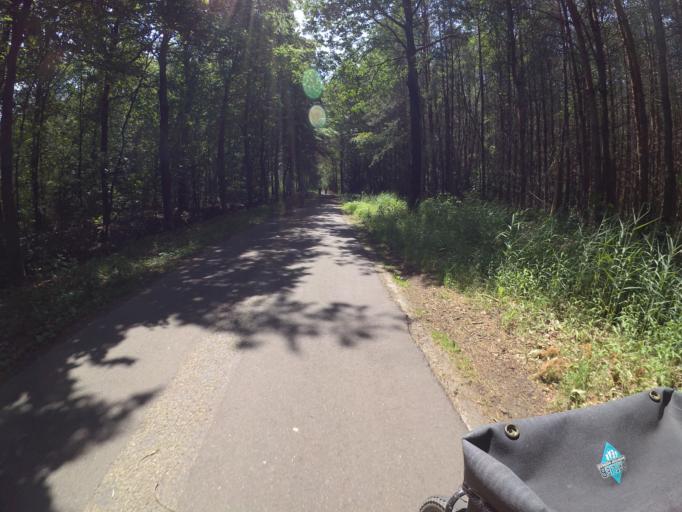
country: NL
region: North Brabant
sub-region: Gemeente Oirschot
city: Middelbeers
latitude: 51.4974
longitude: 5.2498
